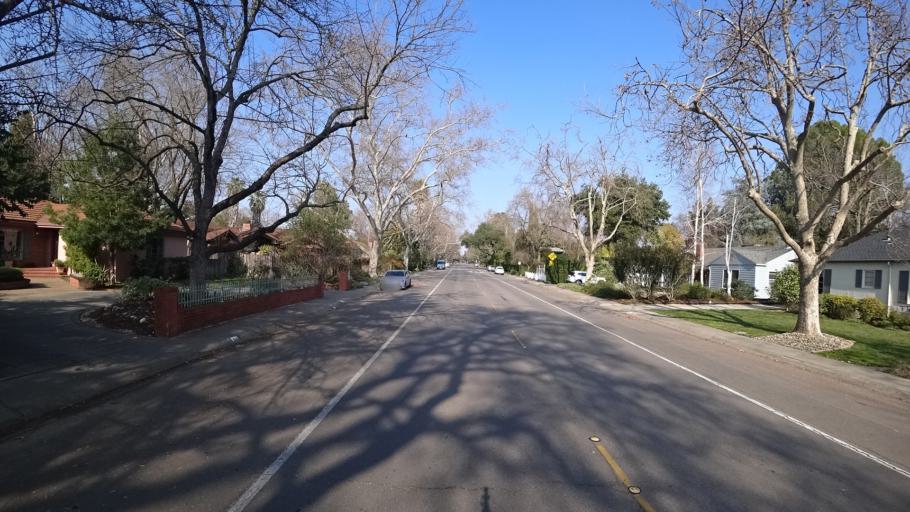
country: US
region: California
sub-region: Yolo County
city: Davis
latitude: 38.5488
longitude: -121.7528
